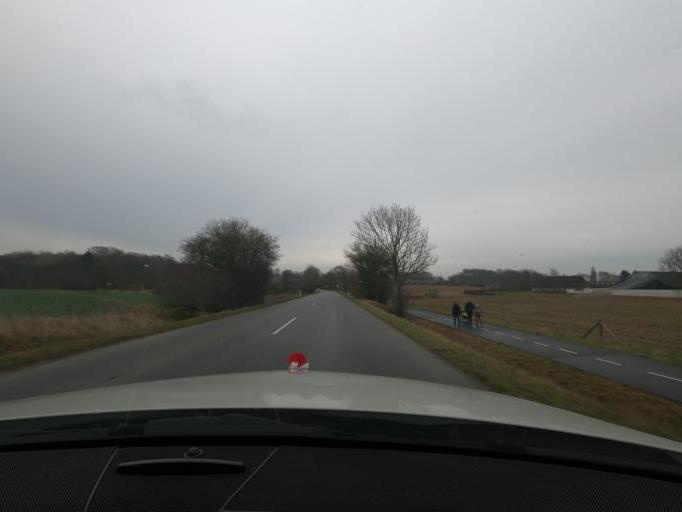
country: DK
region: South Denmark
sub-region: Haderslev Kommune
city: Starup
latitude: 55.1929
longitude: 9.5690
